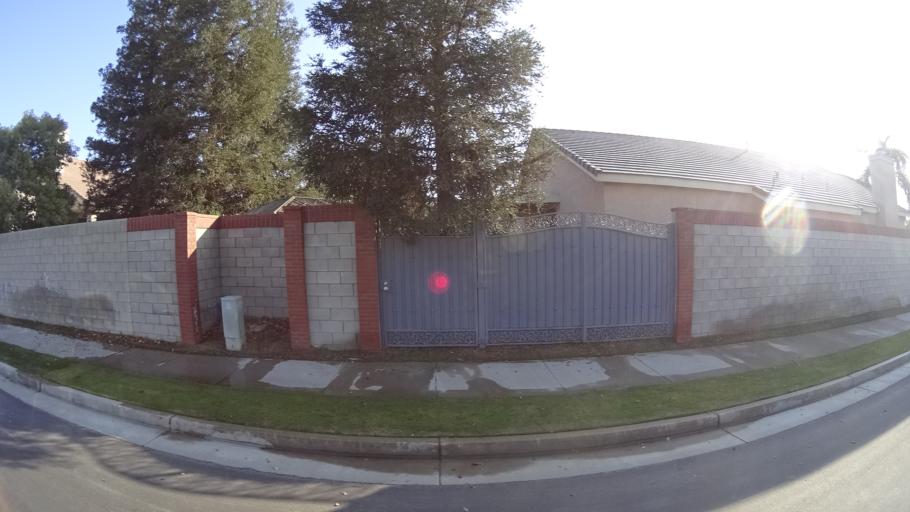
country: US
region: California
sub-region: Kern County
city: Greenacres
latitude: 35.3652
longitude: -119.1249
